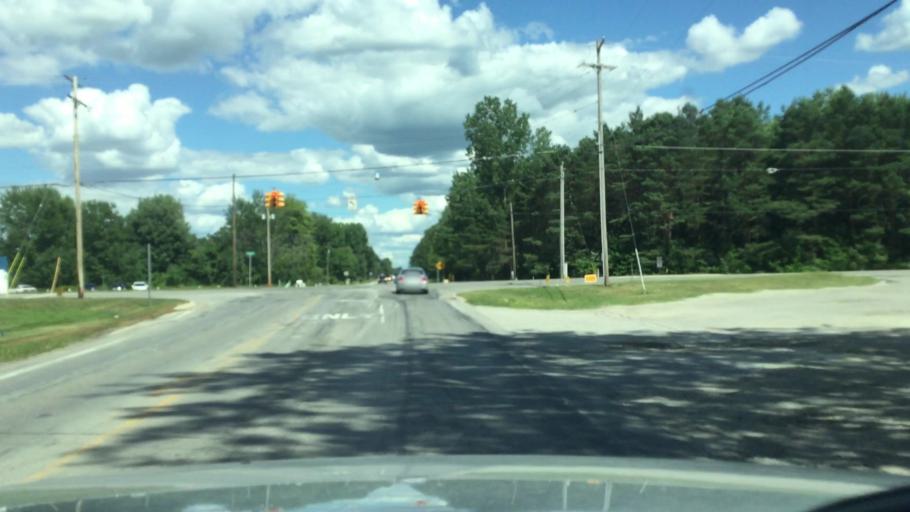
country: US
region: Michigan
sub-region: Saginaw County
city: Saint Charles
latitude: 43.3798
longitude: -84.1318
